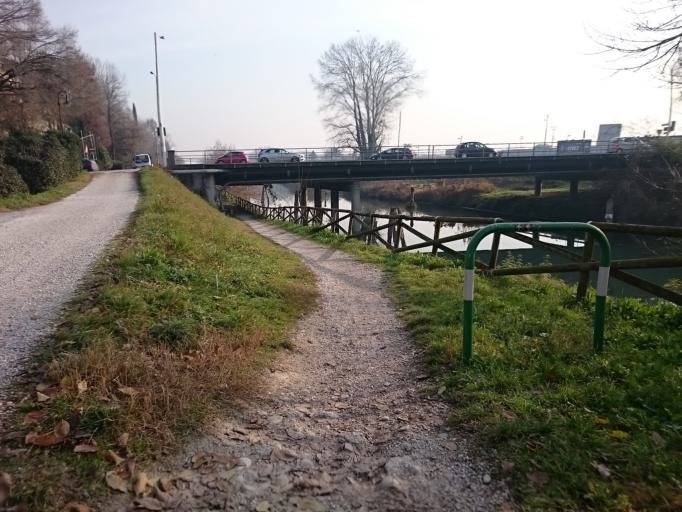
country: IT
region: Veneto
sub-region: Provincia di Padova
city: Padova
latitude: 45.4058
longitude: 11.9005
